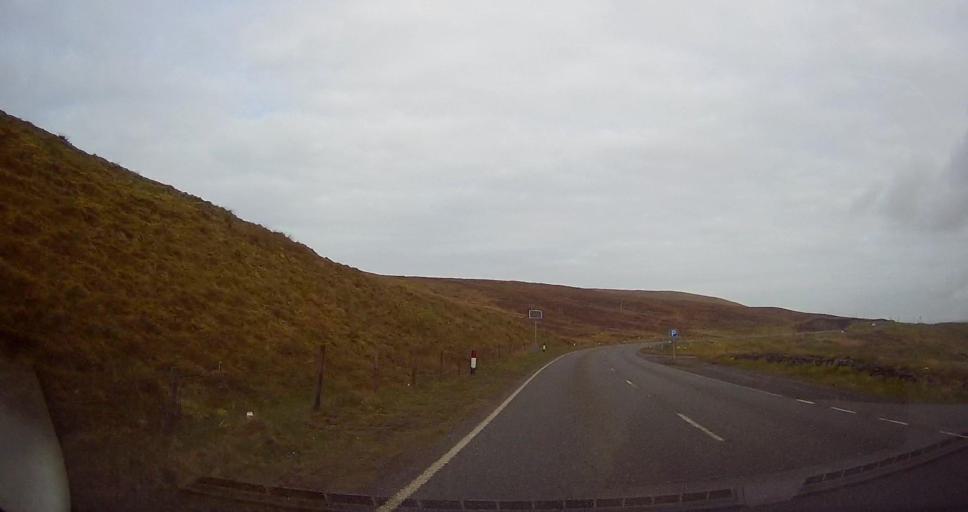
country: GB
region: Scotland
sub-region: Shetland Islands
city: Sandwick
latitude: 60.0699
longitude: -1.2288
